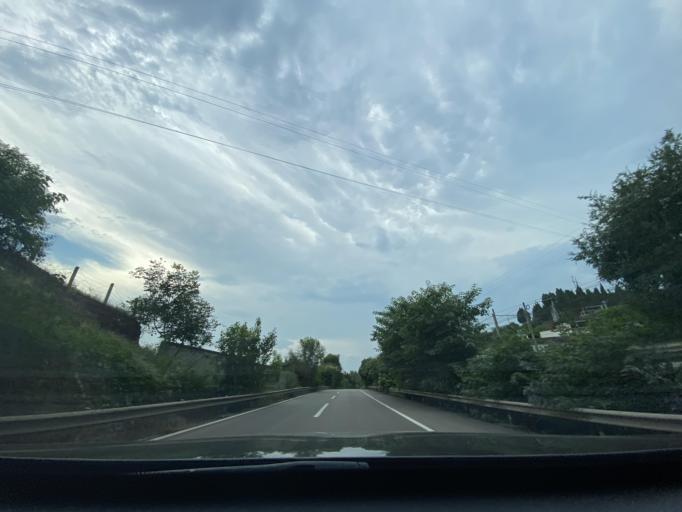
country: CN
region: Sichuan
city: Neijiang
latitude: 29.6791
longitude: 104.9637
